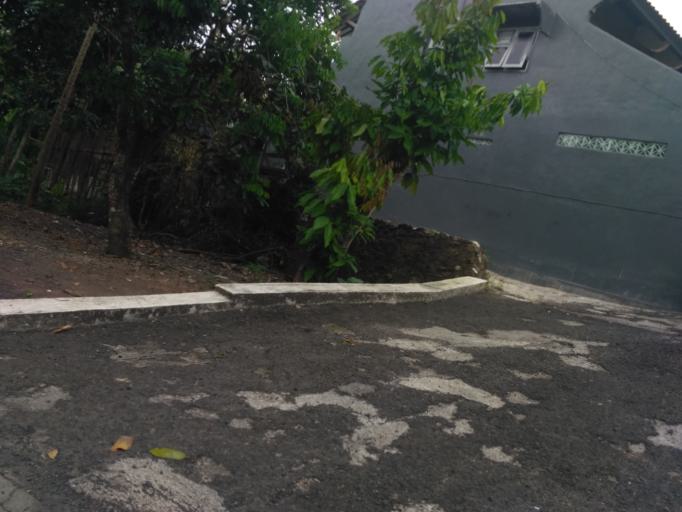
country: ID
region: Central Java
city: Ungaran
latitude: -7.0757
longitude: 110.4290
